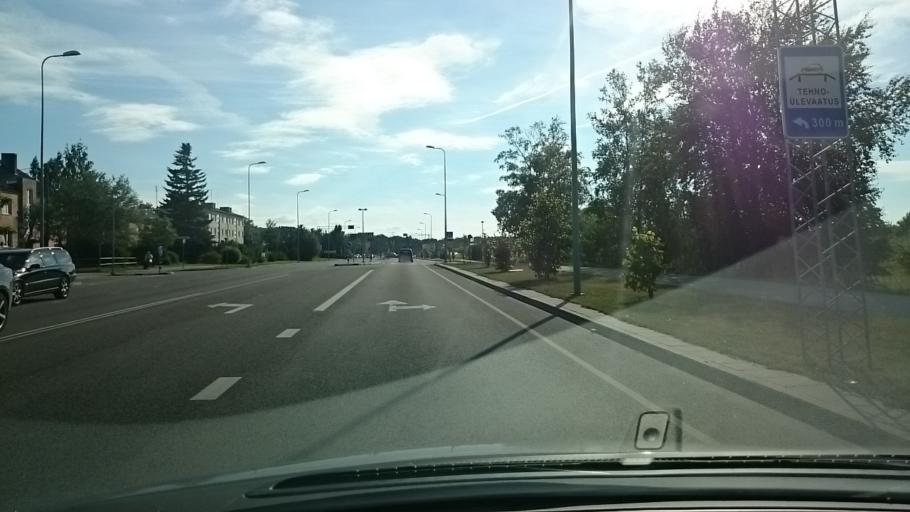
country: EE
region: Laeaene
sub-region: Ridala Parish
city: Uuemoisa
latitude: 58.9401
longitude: 23.5794
